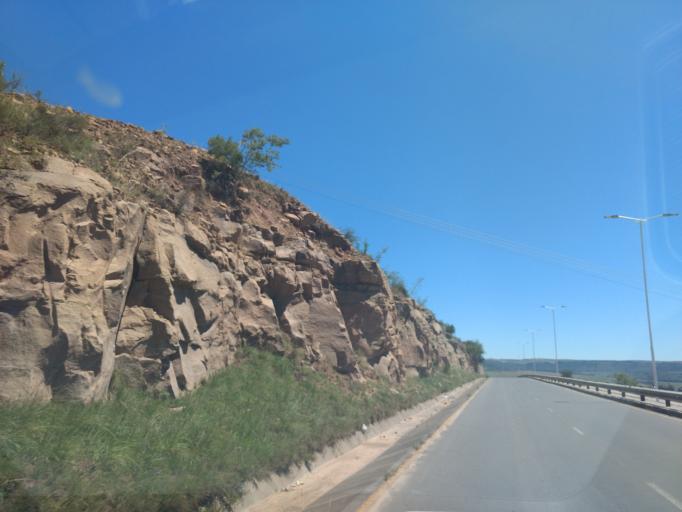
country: LS
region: Maseru
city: Maseru
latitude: -29.3211
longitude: 27.4947
